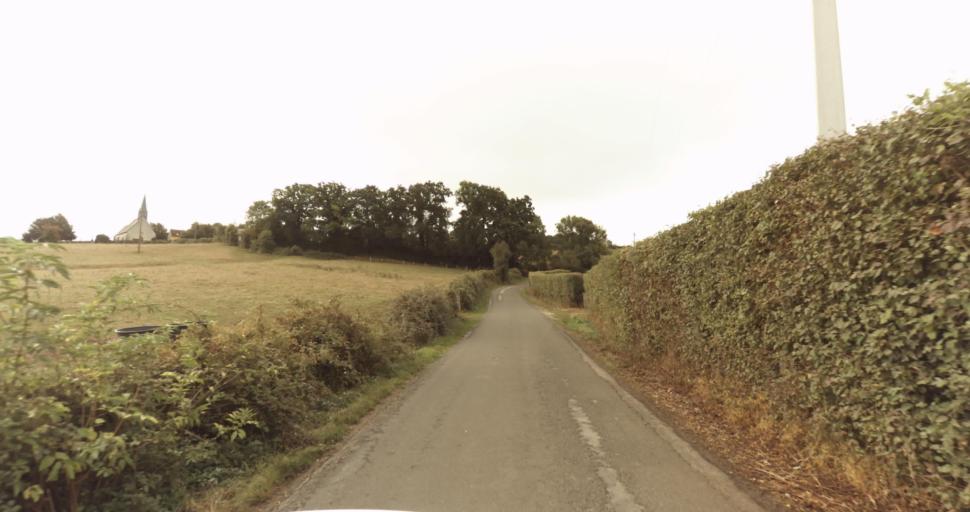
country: FR
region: Lower Normandy
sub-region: Departement de l'Orne
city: Trun
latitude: 48.9109
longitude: 0.1003
